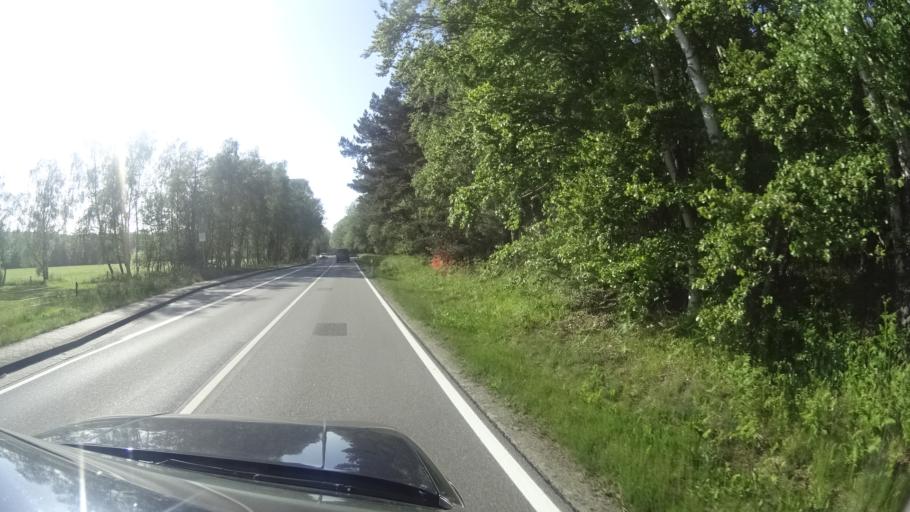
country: DE
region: Mecklenburg-Vorpommern
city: Born
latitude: 54.3990
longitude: 12.4932
